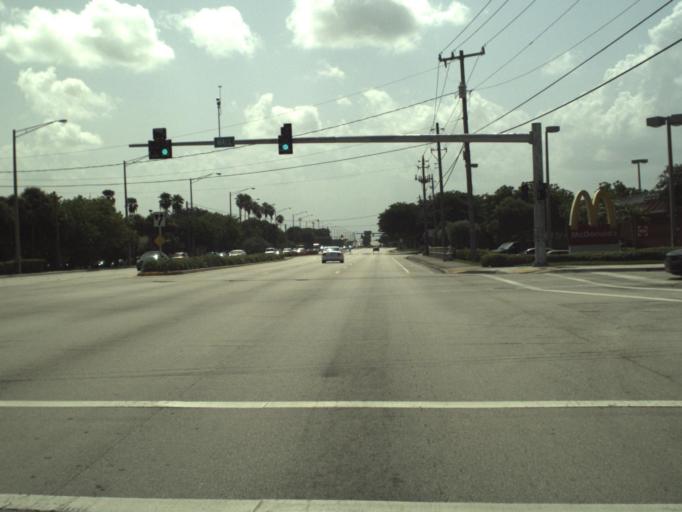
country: US
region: Florida
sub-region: Palm Beach County
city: Boca Pointe
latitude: 26.3180
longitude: -80.1560
